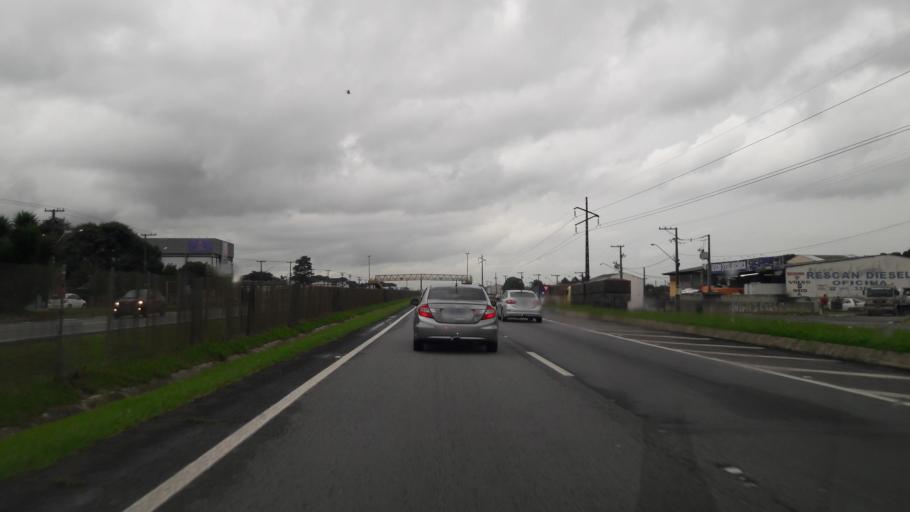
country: BR
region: Parana
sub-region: Piraquara
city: Piraquara
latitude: -25.5302
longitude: -49.0859
